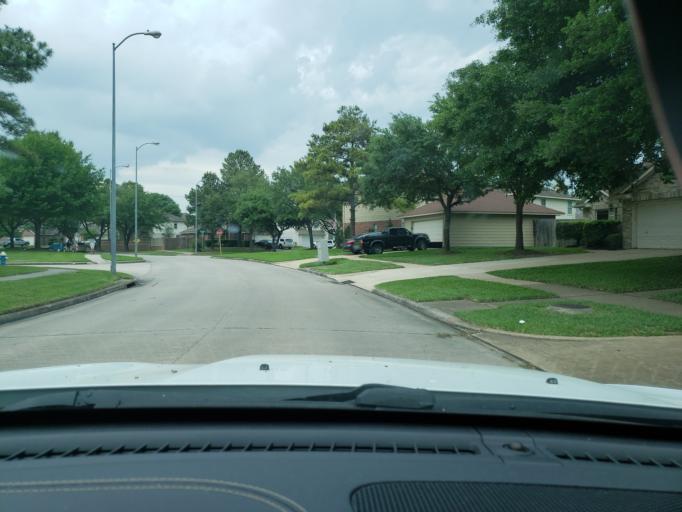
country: US
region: Texas
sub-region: Harris County
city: Jersey Village
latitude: 29.9195
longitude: -95.5755
